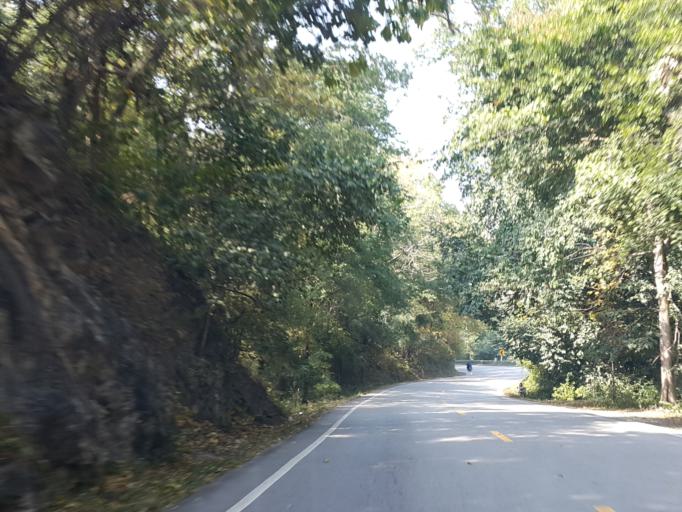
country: TH
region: Chiang Mai
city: Hot
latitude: 18.2220
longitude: 98.4731
